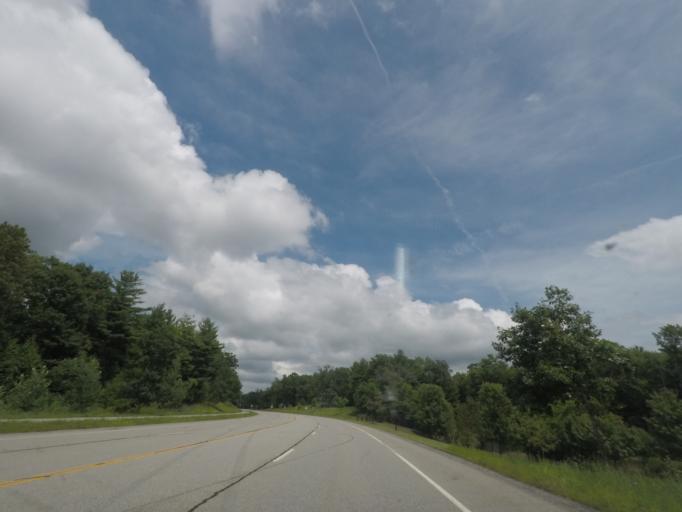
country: US
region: New York
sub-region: Saratoga County
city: Country Knolls
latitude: 42.9558
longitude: -73.7554
